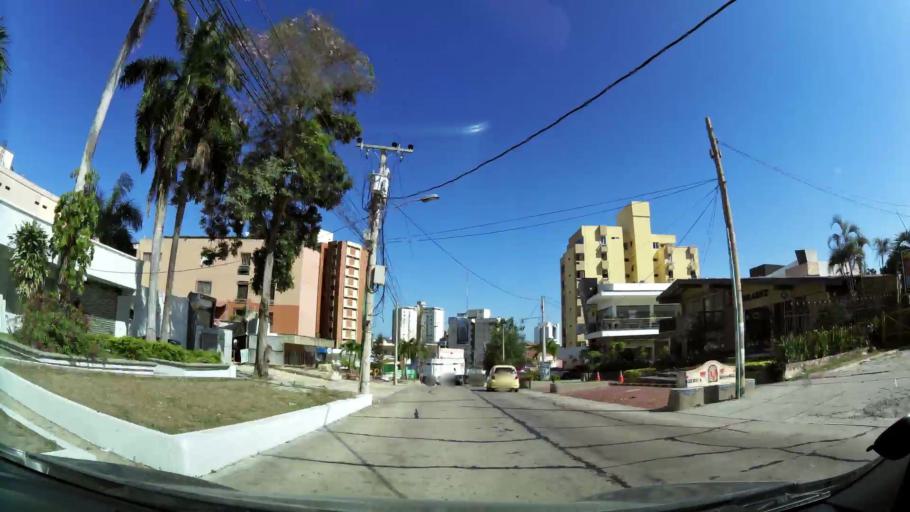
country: CO
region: Atlantico
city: Barranquilla
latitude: 11.0023
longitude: -74.8081
